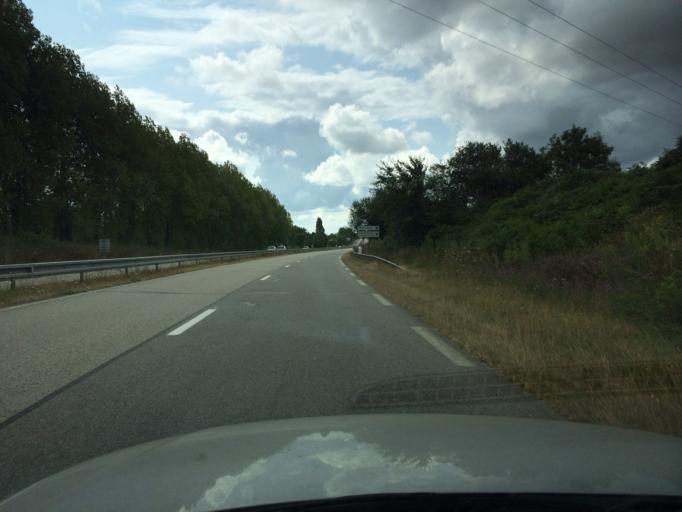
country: FR
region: Lower Normandy
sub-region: Departement de la Manche
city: Valognes
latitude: 49.5172
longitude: -1.4967
